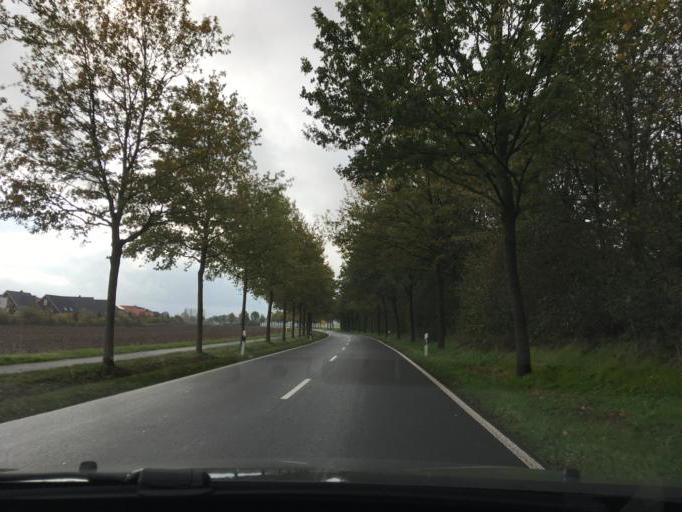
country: DE
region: North Rhine-Westphalia
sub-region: Regierungsbezirk Munster
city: Vreden
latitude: 52.0461
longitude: 6.8045
